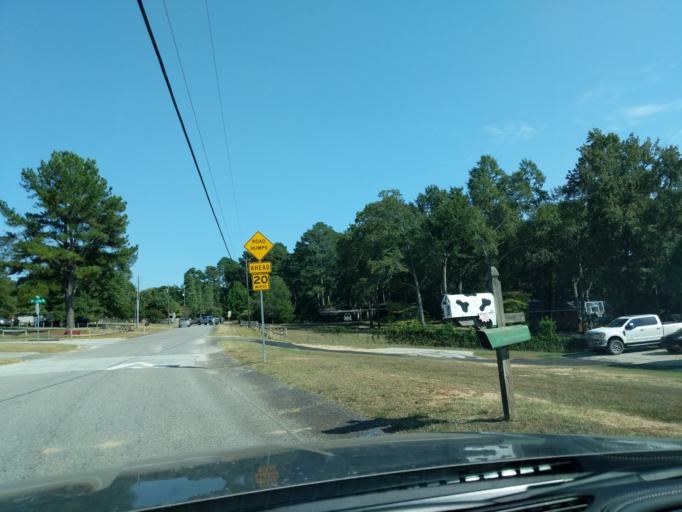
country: US
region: Georgia
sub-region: Columbia County
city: Evans
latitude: 33.5003
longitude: -82.1467
